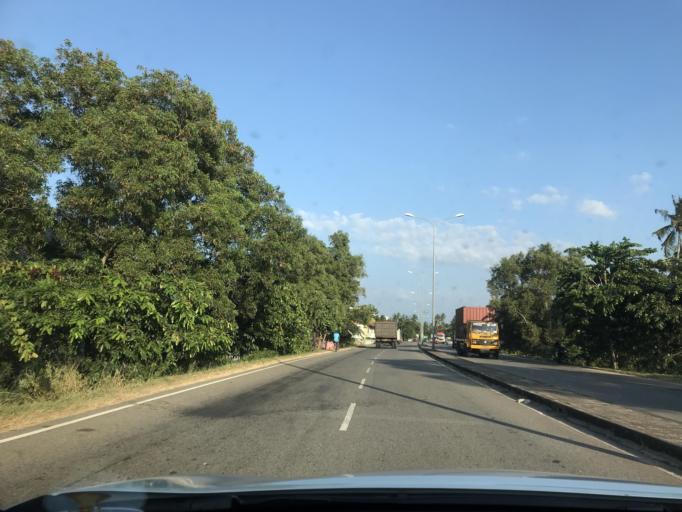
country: LK
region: Western
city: Ja Ela
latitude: 7.0823
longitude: 79.8868
